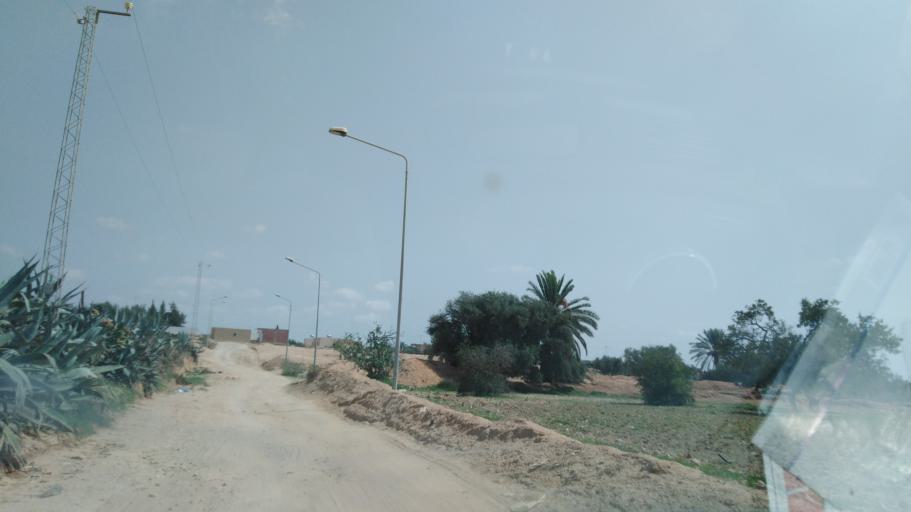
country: TN
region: Safaqis
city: Sfax
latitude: 34.6397
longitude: 10.6159
